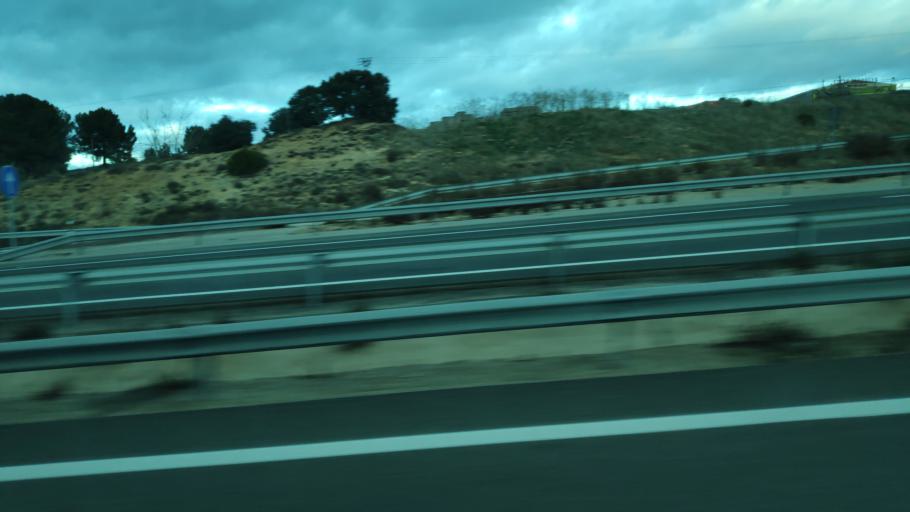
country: ES
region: Castille-La Mancha
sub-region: Provincia de Cuenca
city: Tarancon
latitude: 40.0148
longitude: -3.0312
